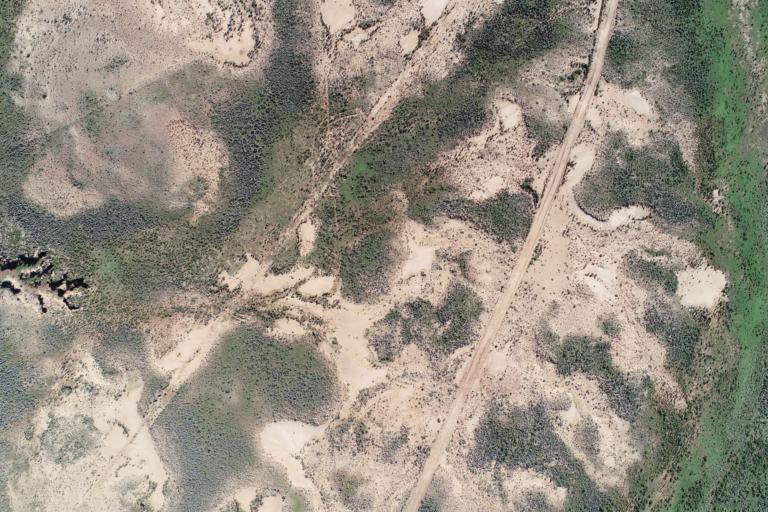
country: BO
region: La Paz
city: Curahuara de Carangas
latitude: -17.3035
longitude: -68.5123
